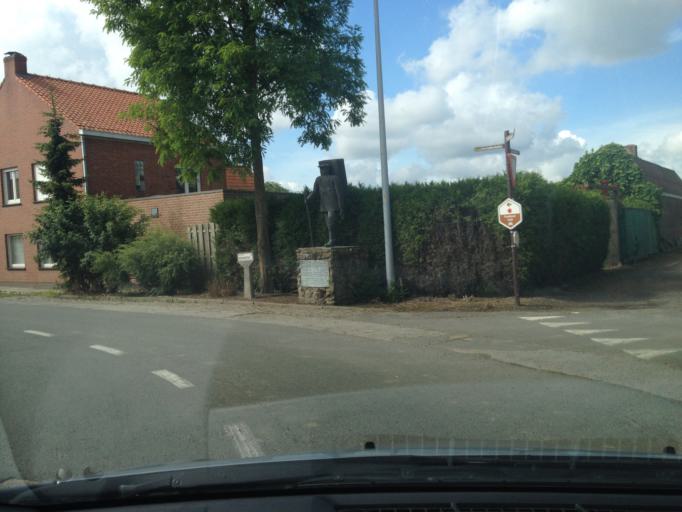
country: FR
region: Nord-Pas-de-Calais
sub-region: Departement du Nord
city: Killem
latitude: 50.9055
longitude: 2.6168
